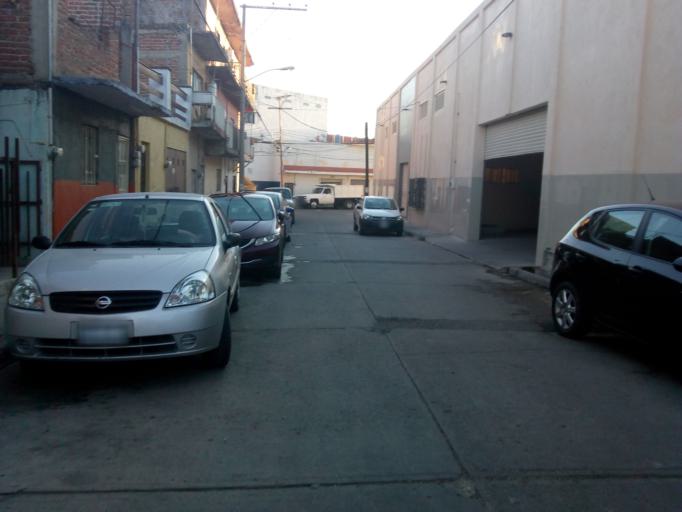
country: MX
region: Guanajuato
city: Leon
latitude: 21.1381
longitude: -101.6814
